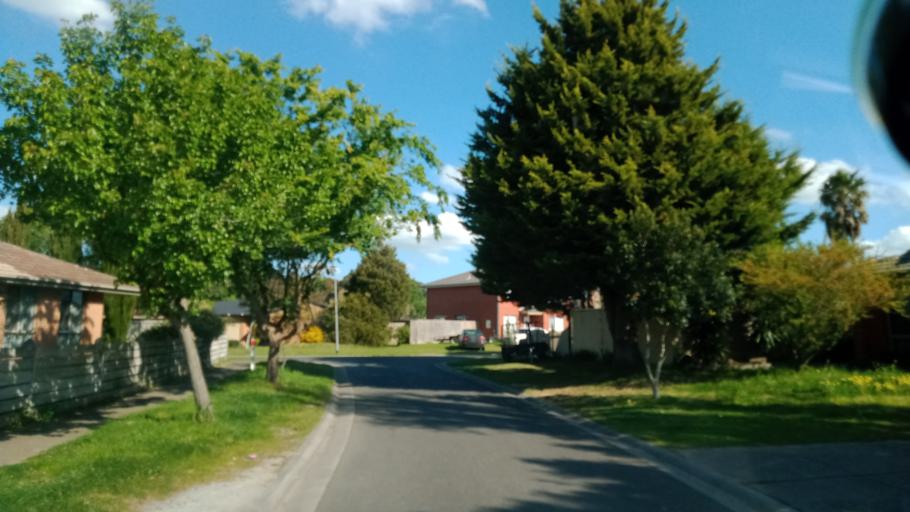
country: AU
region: Victoria
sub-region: Casey
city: Cranbourne West
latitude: -38.0977
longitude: 145.2665
